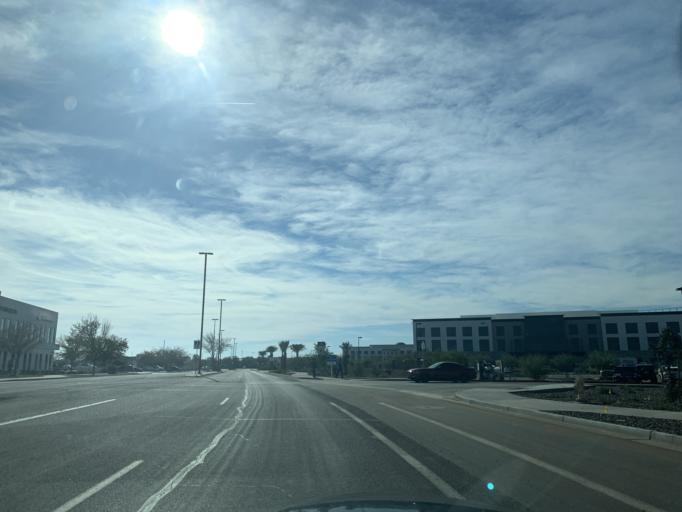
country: US
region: Arizona
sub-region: Maricopa County
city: Gilbert
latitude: 33.2904
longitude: -111.7484
